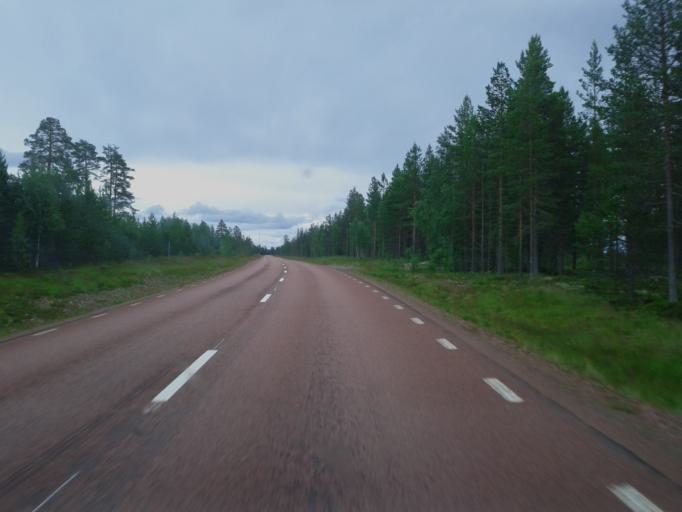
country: SE
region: Dalarna
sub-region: Alvdalens Kommun
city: AElvdalen
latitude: 61.5535
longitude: 13.3227
